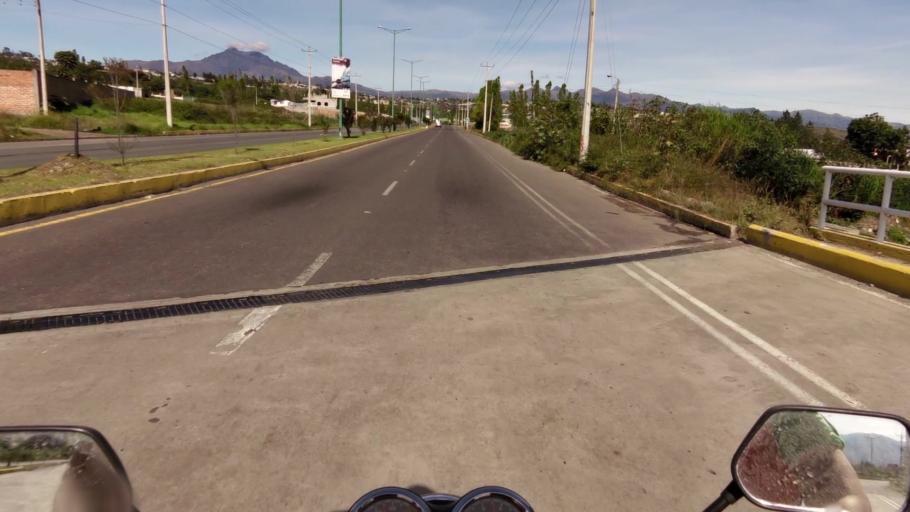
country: EC
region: Imbabura
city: Ibarra
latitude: 0.3315
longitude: -78.1527
